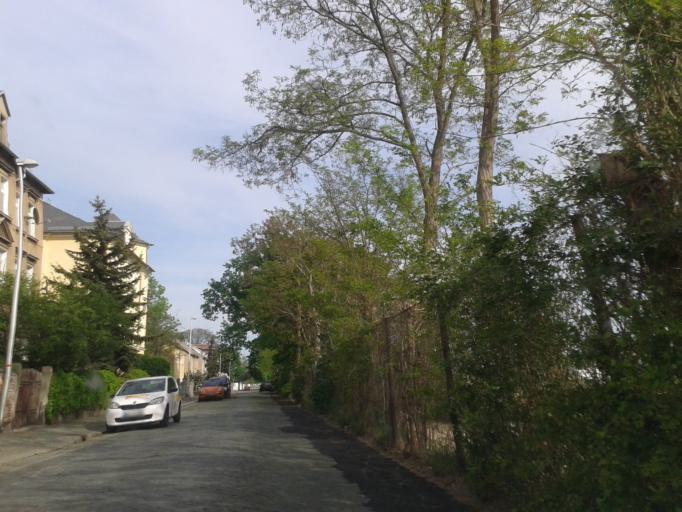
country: DE
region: Saxony
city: Radebeul
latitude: 51.0982
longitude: 13.6832
